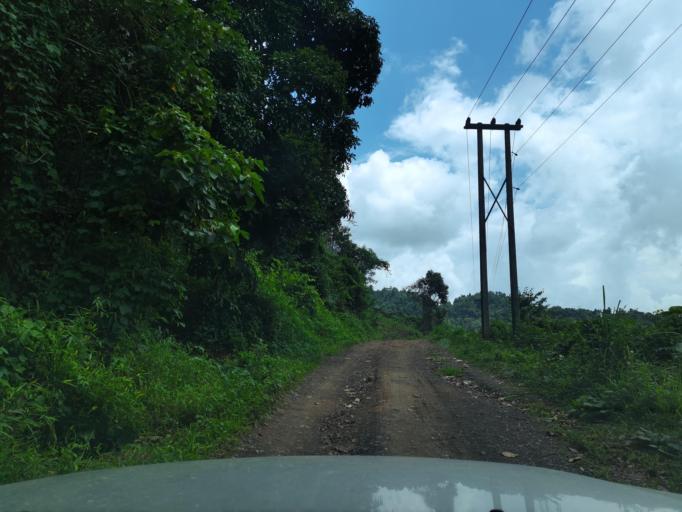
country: LA
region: Loungnamtha
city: Muang Long
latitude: 20.7469
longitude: 101.0188
